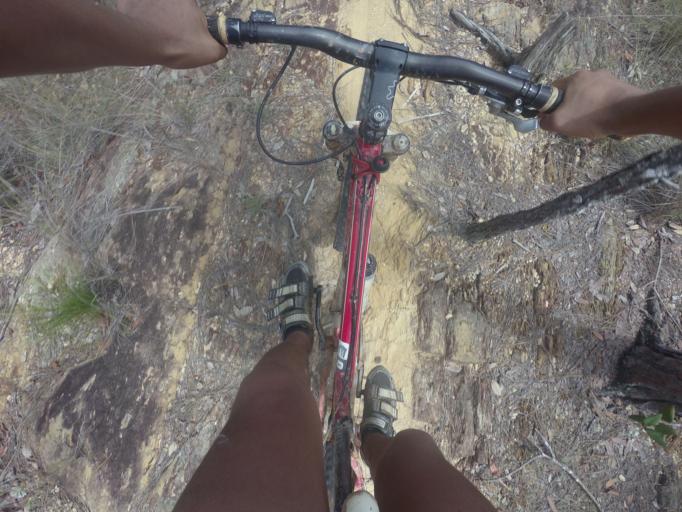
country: CU
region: Pinar del Rio
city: Vinales
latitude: 22.5803
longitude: -83.7716
